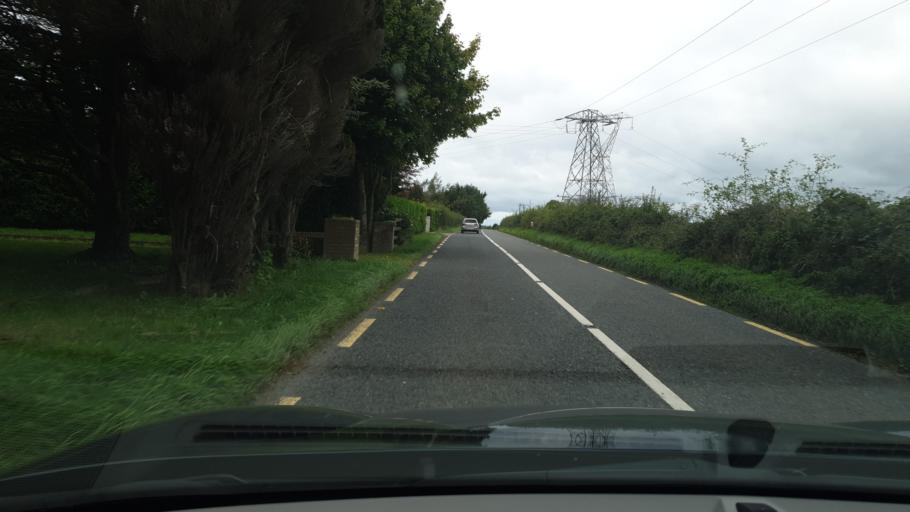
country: IE
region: Leinster
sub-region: Kildare
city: Naas
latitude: 53.2226
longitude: -6.7039
